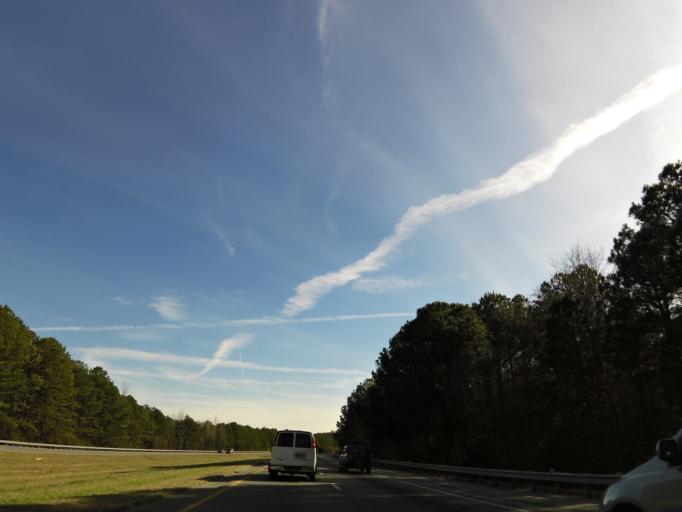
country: US
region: Alabama
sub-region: Russell County
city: Phenix City
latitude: 32.6202
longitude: -84.9527
